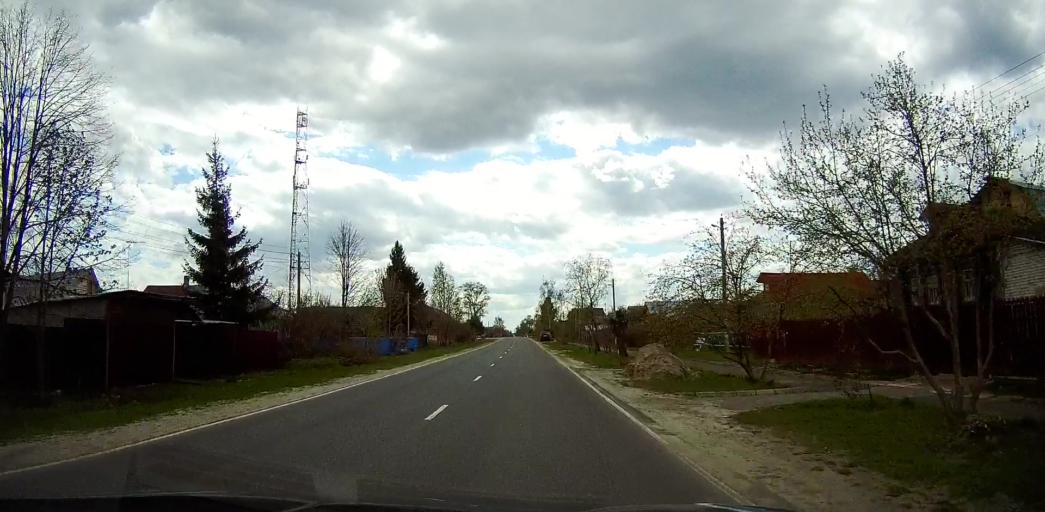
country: RU
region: Moskovskaya
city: Drezna
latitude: 55.6698
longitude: 38.7655
